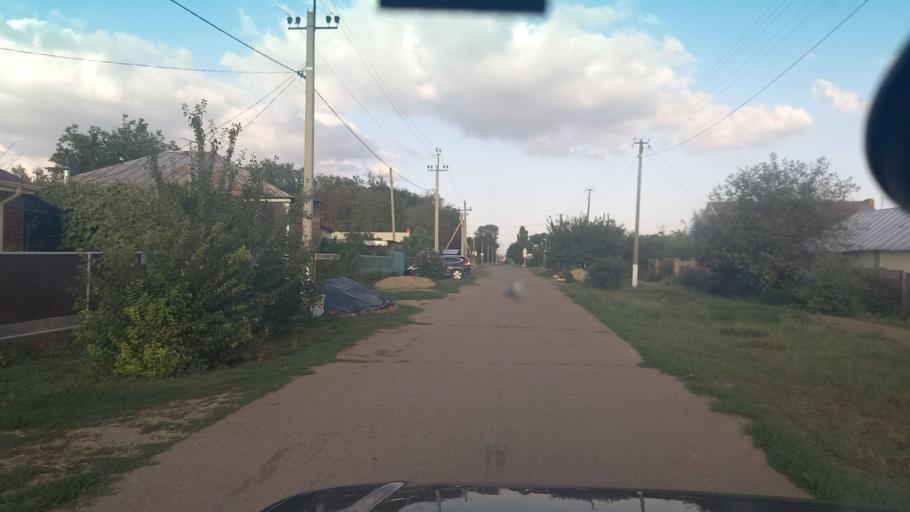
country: RU
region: Adygeya
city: Khatukay
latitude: 45.2942
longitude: 39.5594
